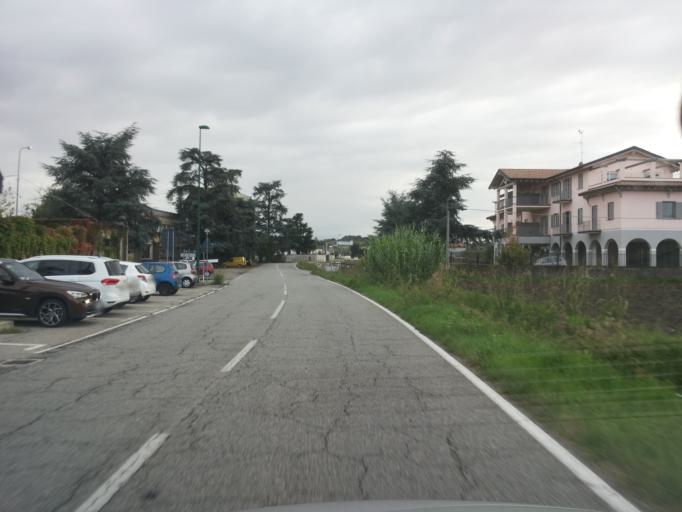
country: IT
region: Piedmont
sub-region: Provincia di Alessandria
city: Casale Monferrato
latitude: 45.1197
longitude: 8.4441
